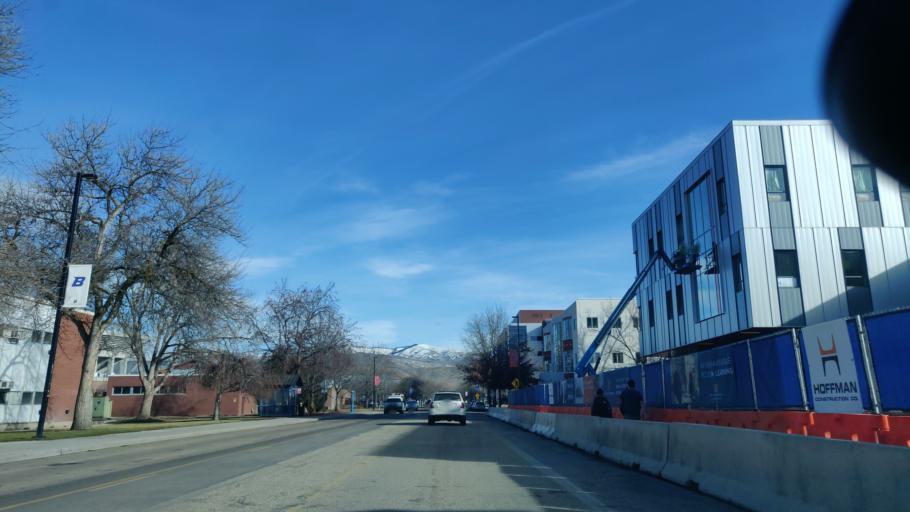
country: US
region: Idaho
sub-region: Ada County
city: Boise
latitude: 43.6010
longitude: -116.1996
